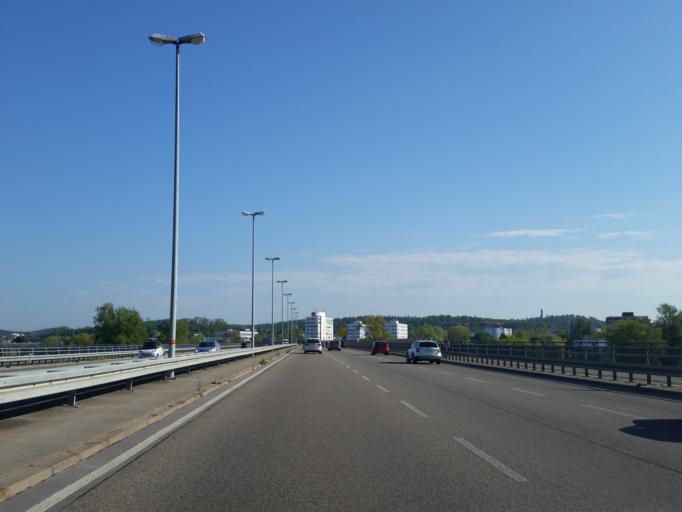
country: DE
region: Baden-Wuerttemberg
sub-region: Freiburg Region
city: Konstanz
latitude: 47.6695
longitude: 9.1629
